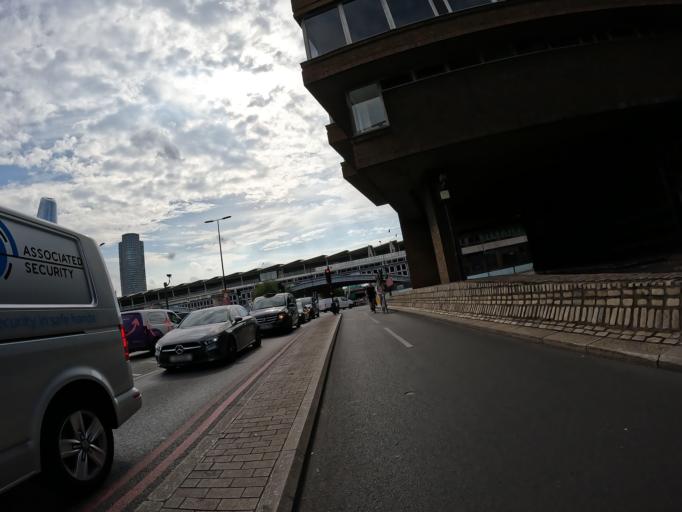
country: GB
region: England
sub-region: Greater London
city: Harringay
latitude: 51.5805
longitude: -0.0885
